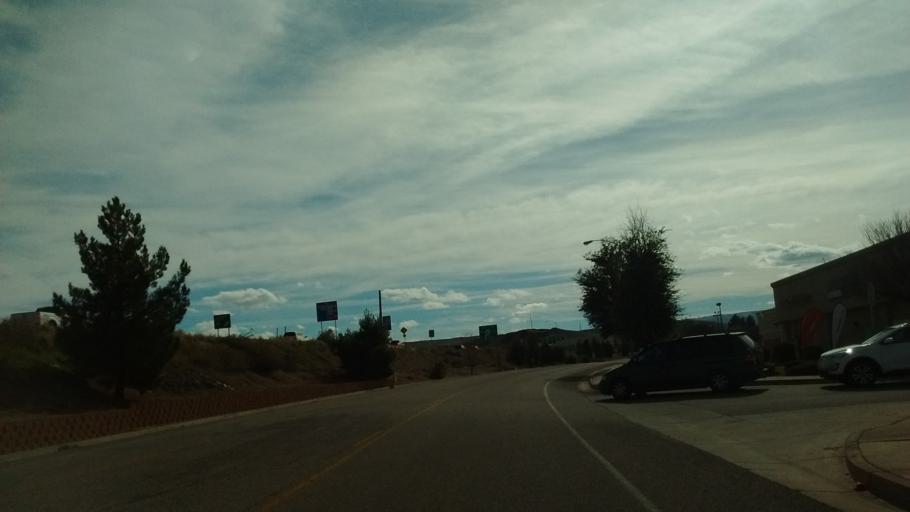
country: US
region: Utah
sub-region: Washington County
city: Saint George
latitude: 37.0637
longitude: -113.5845
